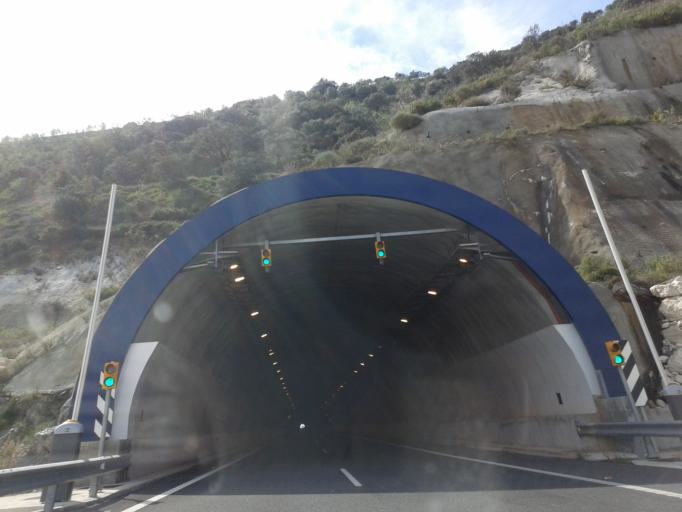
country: ES
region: Andalusia
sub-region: Provincia de Malaga
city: Casabermeja
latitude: 36.8703
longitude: -4.4836
